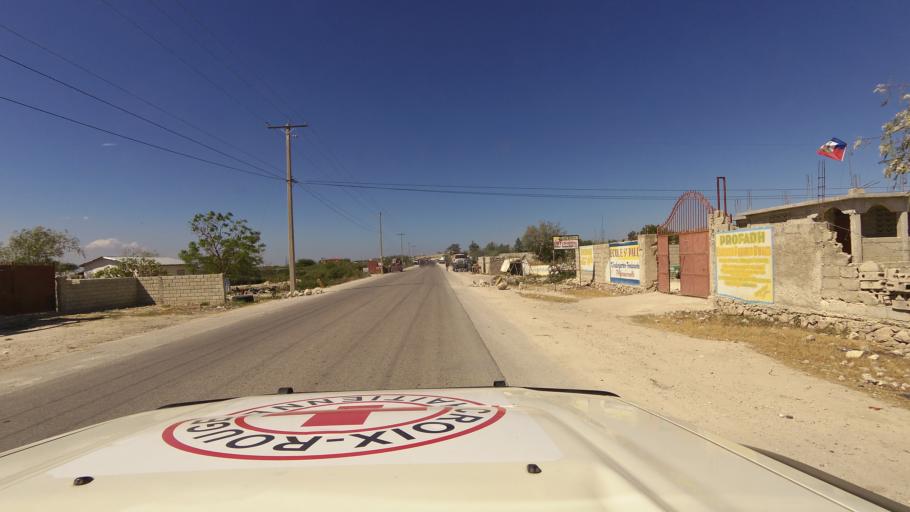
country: HT
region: Ouest
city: Croix des Bouquets
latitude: 18.6486
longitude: -72.2544
